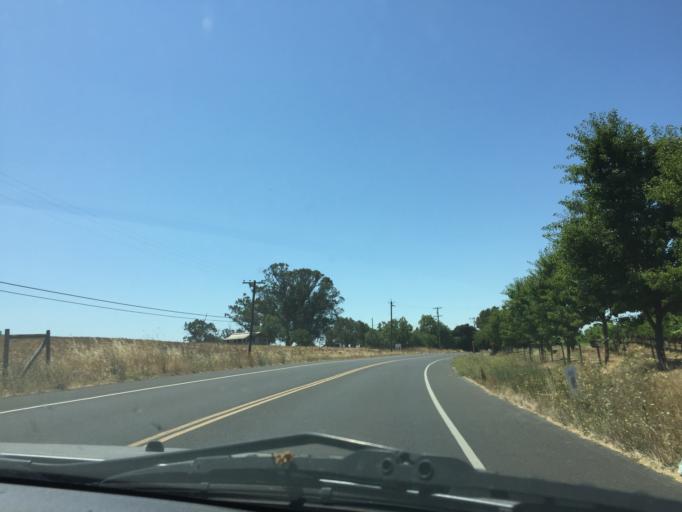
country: US
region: California
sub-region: Napa County
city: Napa
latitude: 38.2613
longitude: -122.3349
